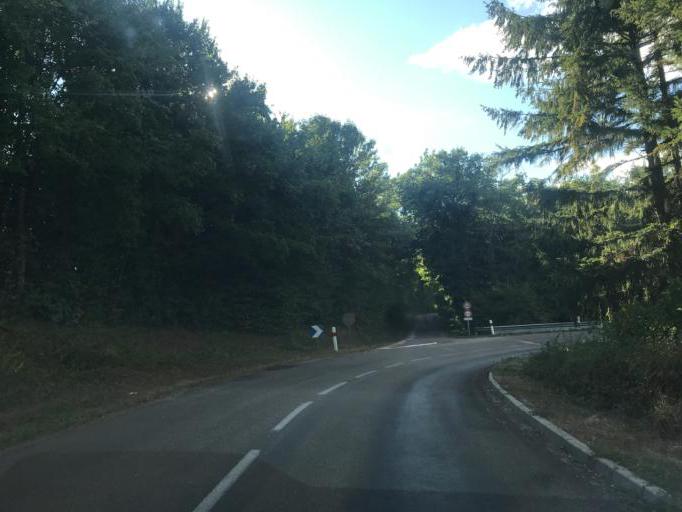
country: FR
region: Bourgogne
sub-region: Departement de l'Yonne
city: Fontenailles
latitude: 47.5971
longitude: 3.4742
